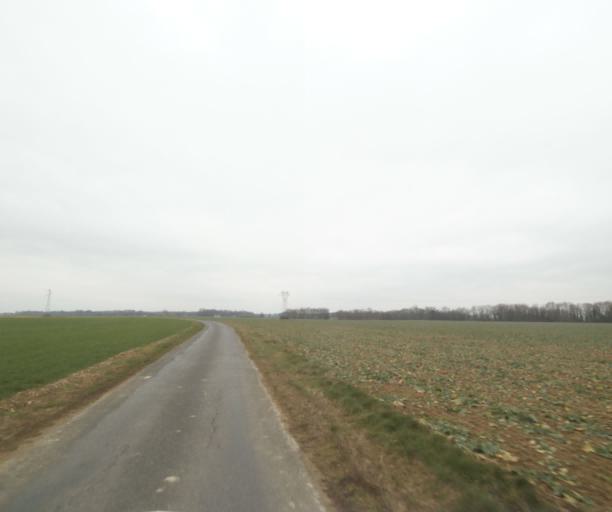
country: FR
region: Champagne-Ardenne
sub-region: Departement de la Haute-Marne
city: Villiers-en-Lieu
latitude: 48.6337
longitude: 4.8287
